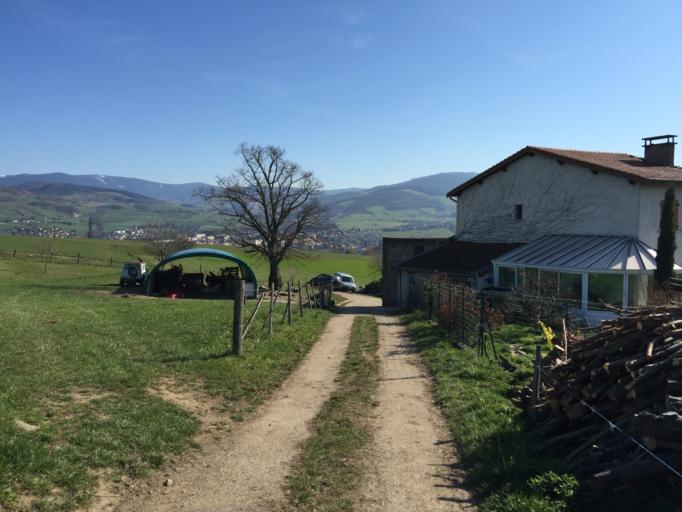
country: FR
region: Rhone-Alpes
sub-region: Departement de la Loire
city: Saint-Chamond
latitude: 45.4815
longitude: 4.4969
